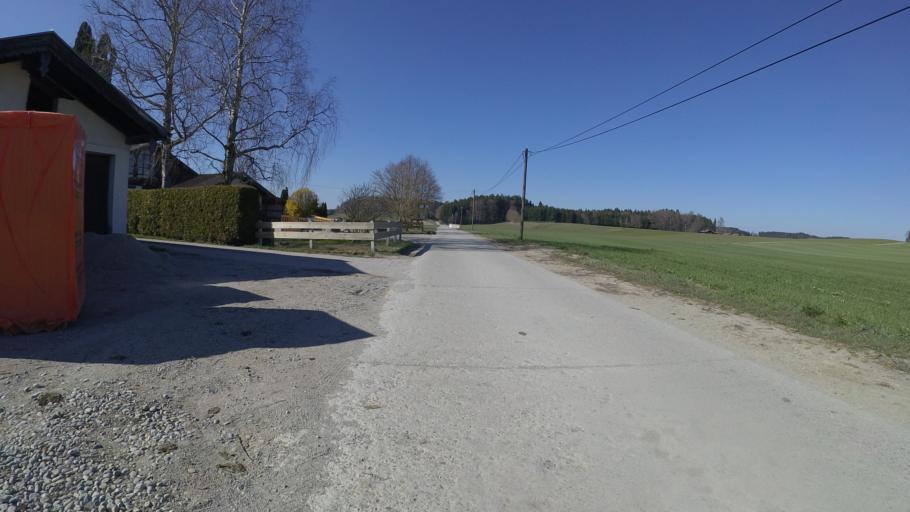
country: DE
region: Bavaria
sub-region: Upper Bavaria
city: Seeon-Seebruck
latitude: 47.9546
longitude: 12.5154
